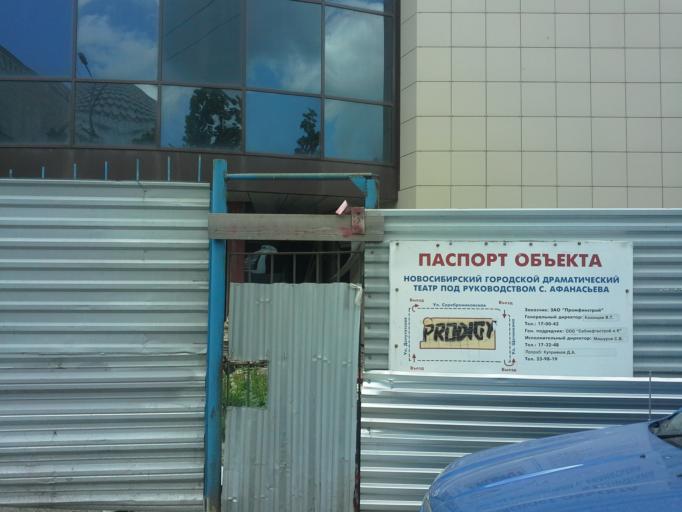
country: RU
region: Novosibirsk
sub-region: Novosibirskiy Rayon
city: Novosibirsk
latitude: 55.0293
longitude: 82.9243
